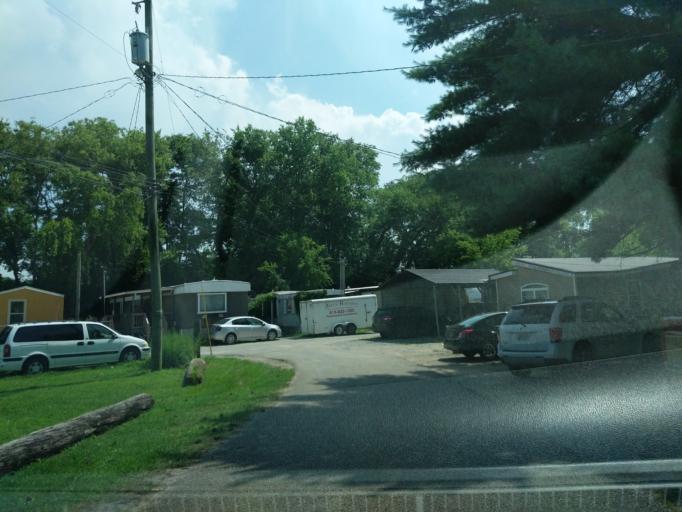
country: US
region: Tennessee
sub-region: Davidson County
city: Goodlettsville
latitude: 36.2847
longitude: -86.6794
